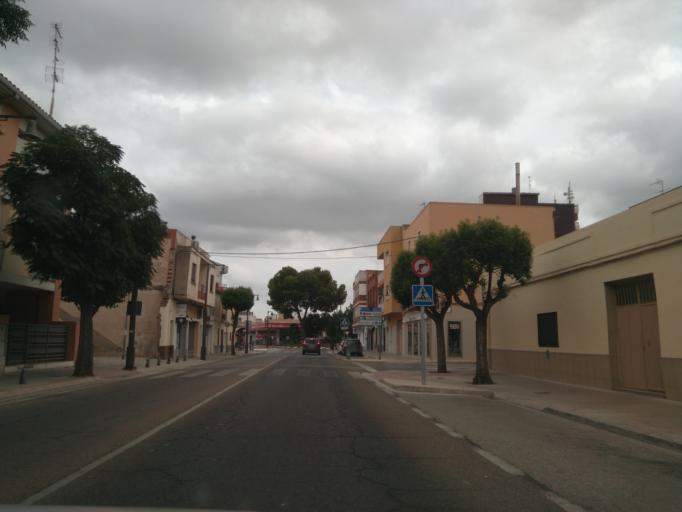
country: ES
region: Valencia
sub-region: Provincia de Valencia
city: L'Alcudia
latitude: 39.2001
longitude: -0.5052
